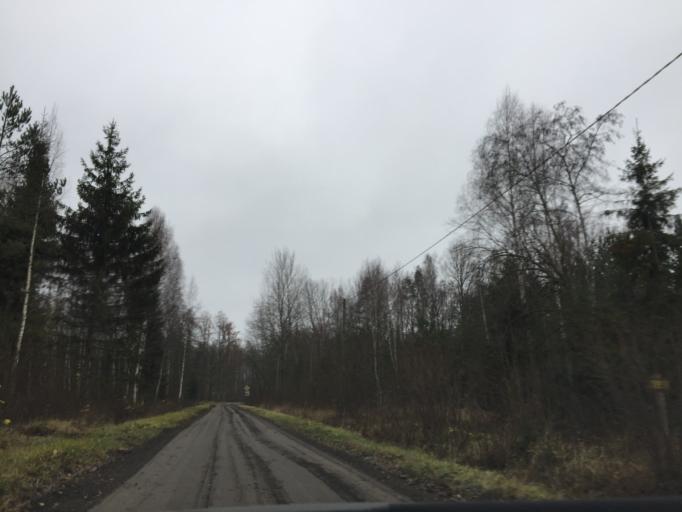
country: LV
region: Limbazu Rajons
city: Limbazi
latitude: 57.4958
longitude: 24.7695
